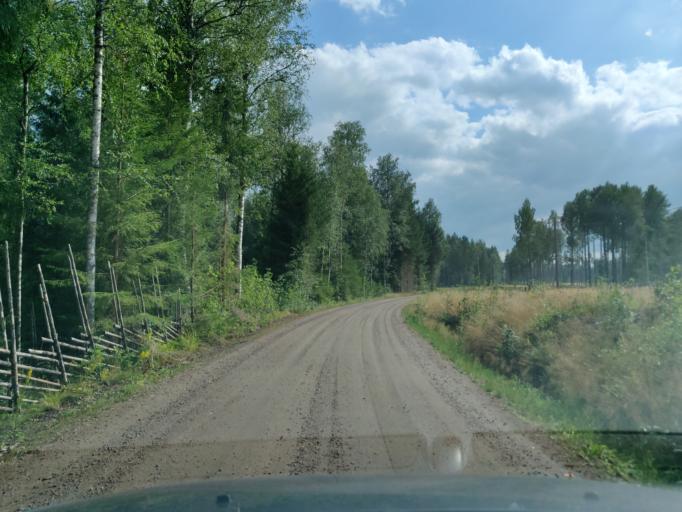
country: SE
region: Vaermland
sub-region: Hagfors Kommun
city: Hagfors
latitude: 59.9940
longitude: 13.5667
